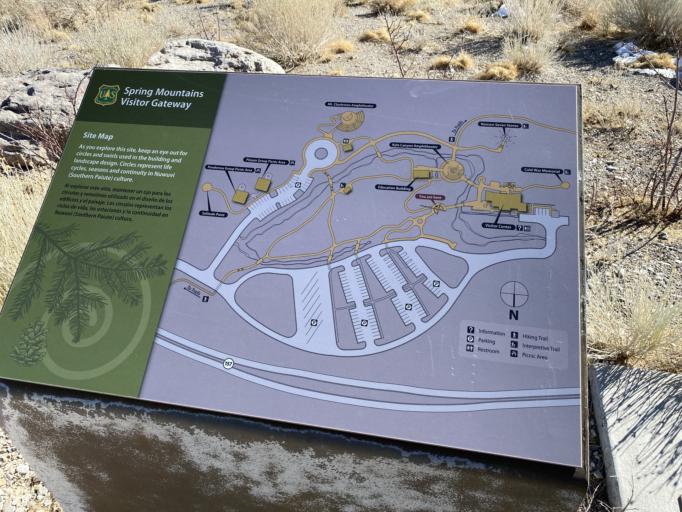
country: US
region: Nevada
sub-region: Clark County
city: Summerlin South
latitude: 36.2708
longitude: -115.5879
